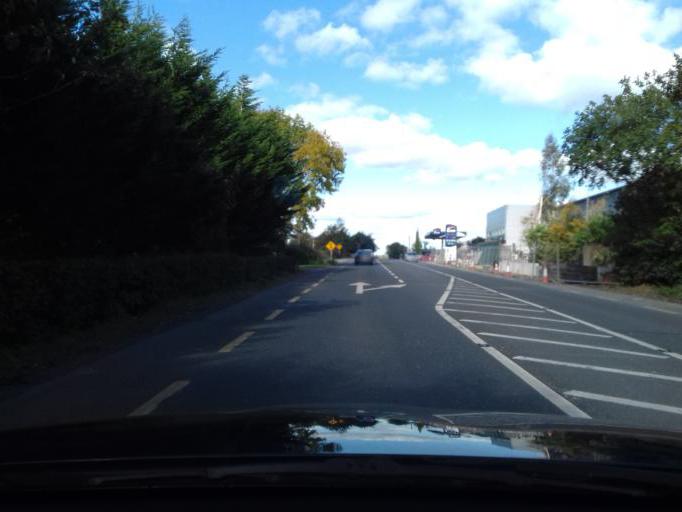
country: IE
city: Kentstown
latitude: 53.6642
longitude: -6.5284
